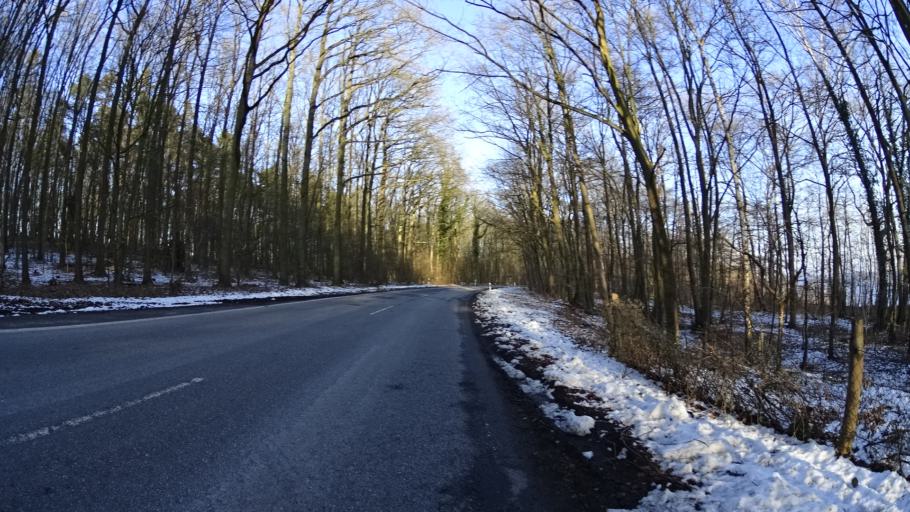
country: DE
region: Schleswig-Holstein
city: Fargau-Pratjau
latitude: 54.3232
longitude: 10.3921
